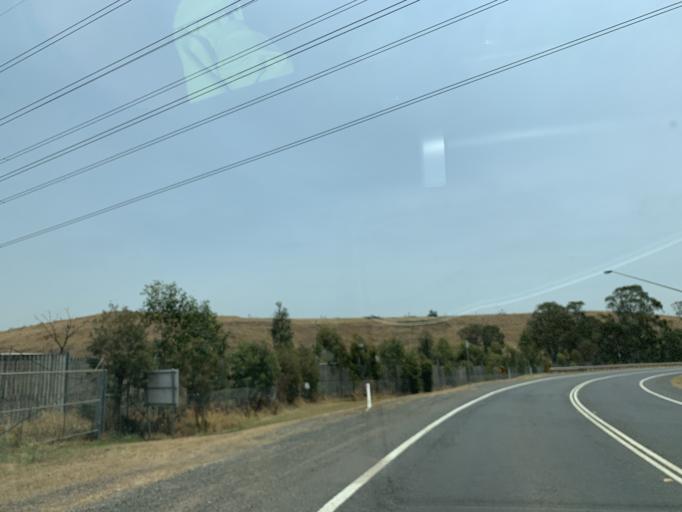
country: AU
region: New South Wales
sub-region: Fairfield
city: Horsley Park
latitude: -33.8151
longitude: 150.8659
